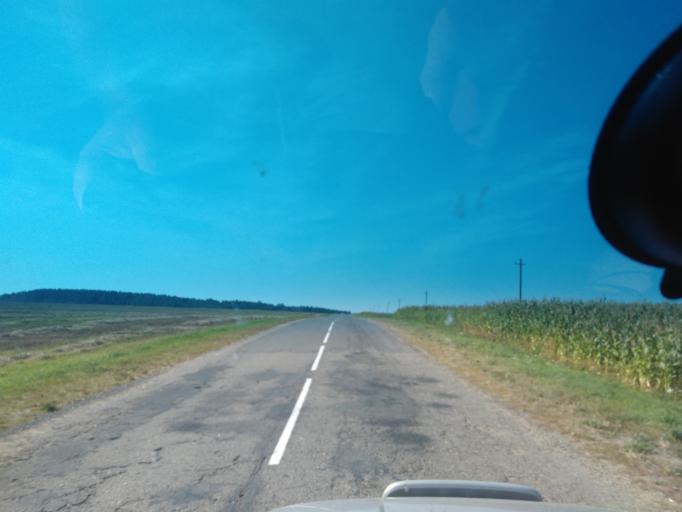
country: BY
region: Minsk
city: Kapyl'
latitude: 53.2210
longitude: 27.1534
